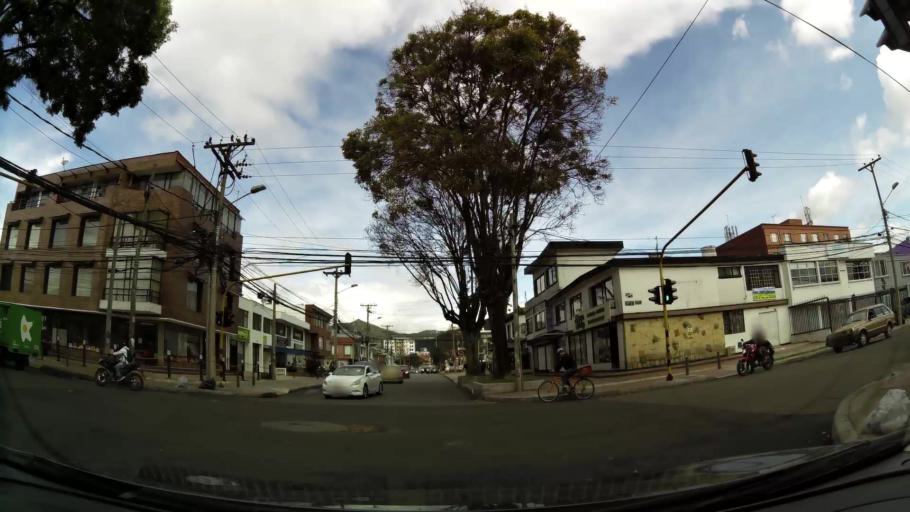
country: CO
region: Bogota D.C.
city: Barrio San Luis
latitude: 4.6842
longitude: -74.0614
